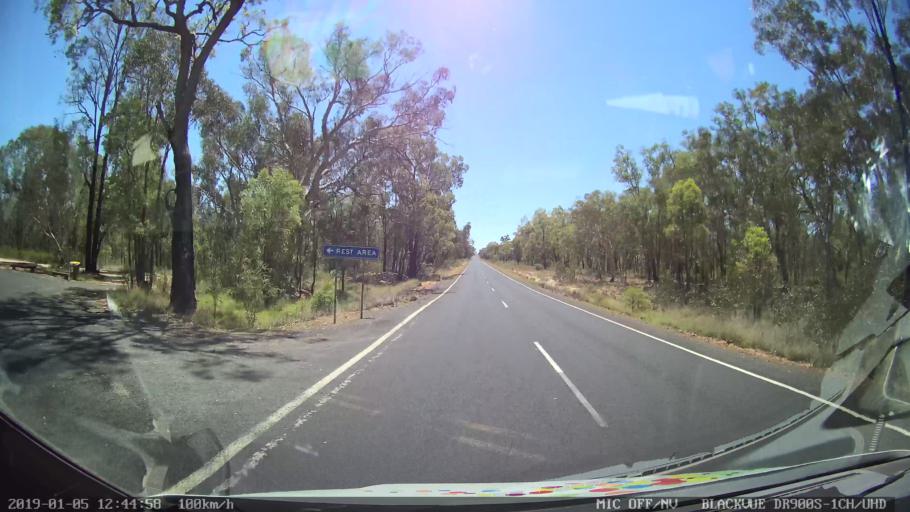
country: AU
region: New South Wales
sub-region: Warrumbungle Shire
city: Coonabarabran
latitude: -31.1325
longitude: 149.5440
